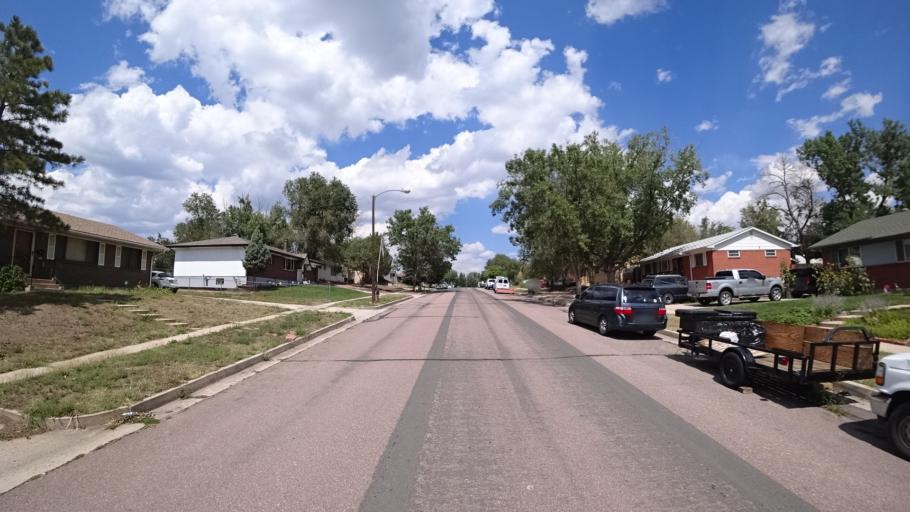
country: US
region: Colorado
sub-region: El Paso County
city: Colorado Springs
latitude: 38.8312
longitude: -104.7799
